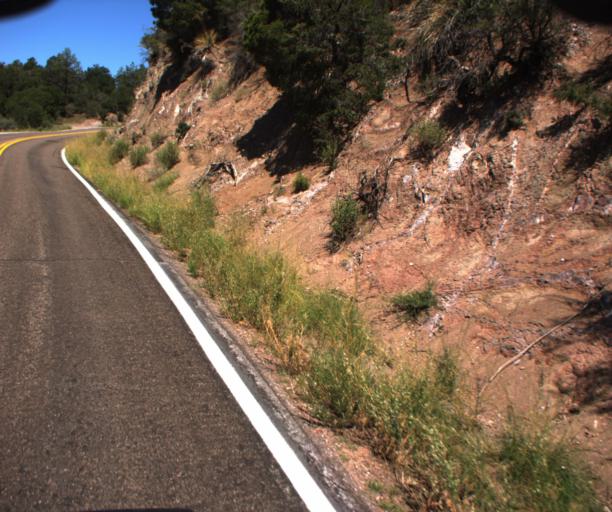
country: US
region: Arizona
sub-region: Greenlee County
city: Morenci
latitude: 33.2140
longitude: -109.3791
